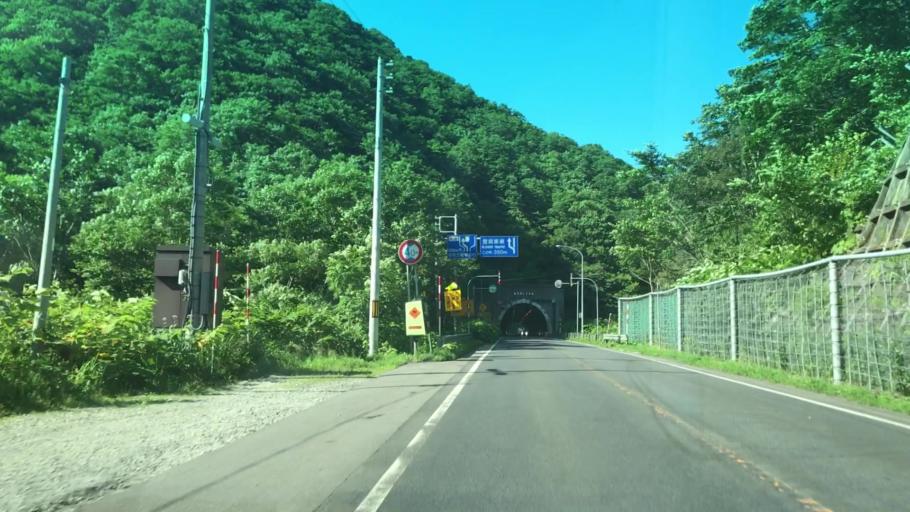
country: JP
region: Hokkaido
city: Iwanai
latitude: 43.0341
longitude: 140.6773
